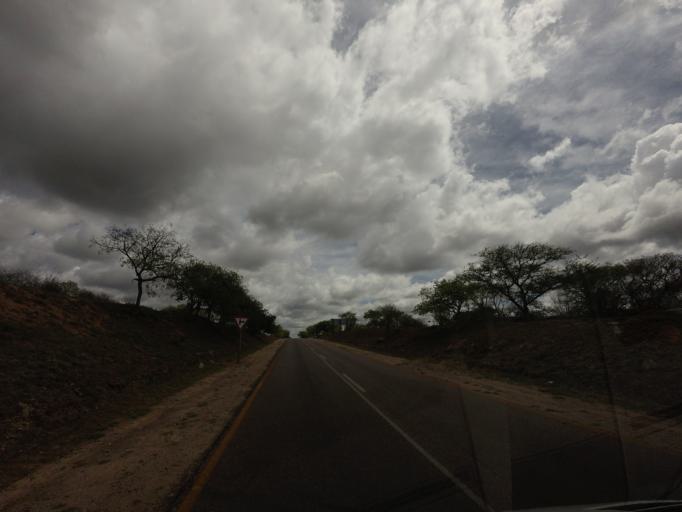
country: ZA
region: Limpopo
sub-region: Mopani District Municipality
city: Hoedspruit
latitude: -24.5525
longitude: 31.0385
